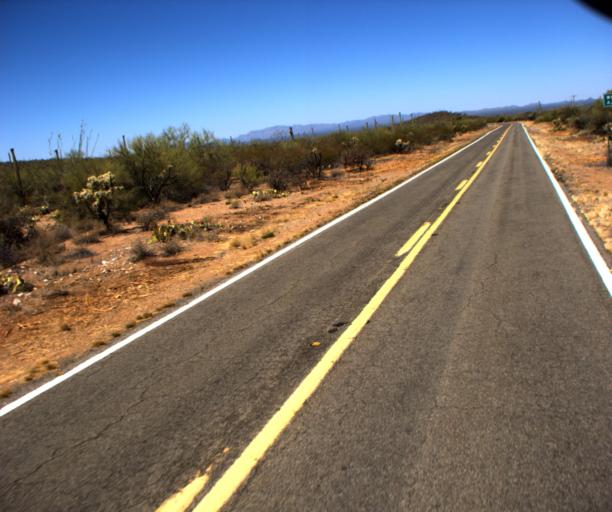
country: US
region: Arizona
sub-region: Pima County
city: Sells
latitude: 32.1771
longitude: -112.2530
